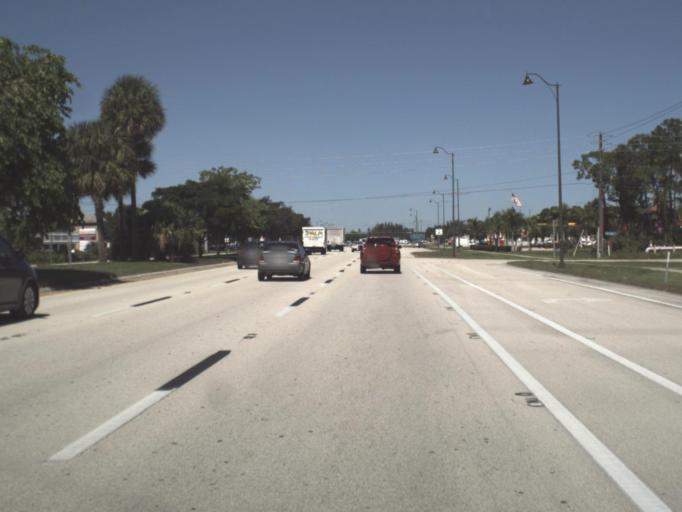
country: US
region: Florida
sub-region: Lee County
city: Bonita Springs
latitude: 26.3755
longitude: -81.8077
